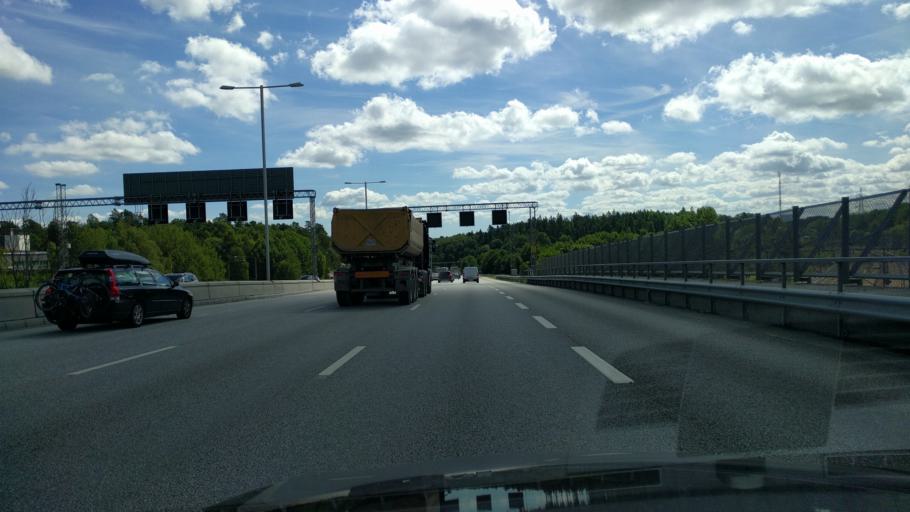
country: SE
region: Stockholm
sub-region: Solna Kommun
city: Rasunda
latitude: 59.3937
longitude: 17.9870
